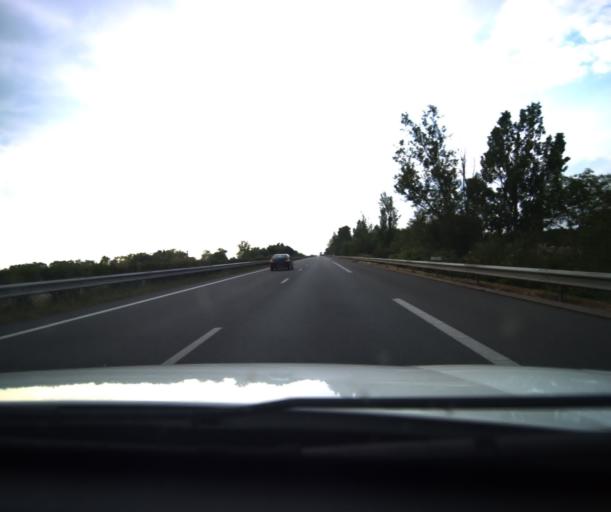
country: FR
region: Midi-Pyrenees
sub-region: Departement du Tarn-et-Garonne
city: Saint-Porquier
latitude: 44.0308
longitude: 1.1622
